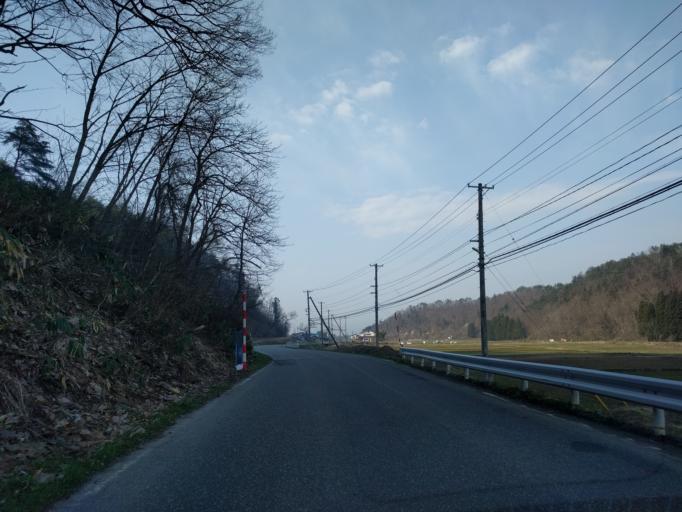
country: JP
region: Fukushima
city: Kitakata
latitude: 37.6918
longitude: 139.9083
